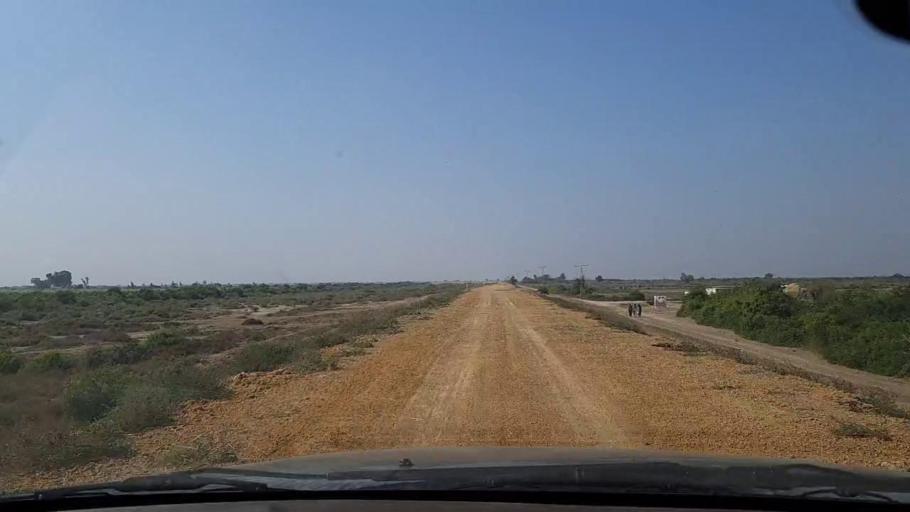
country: PK
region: Sindh
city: Chuhar Jamali
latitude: 24.4618
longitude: 67.8926
